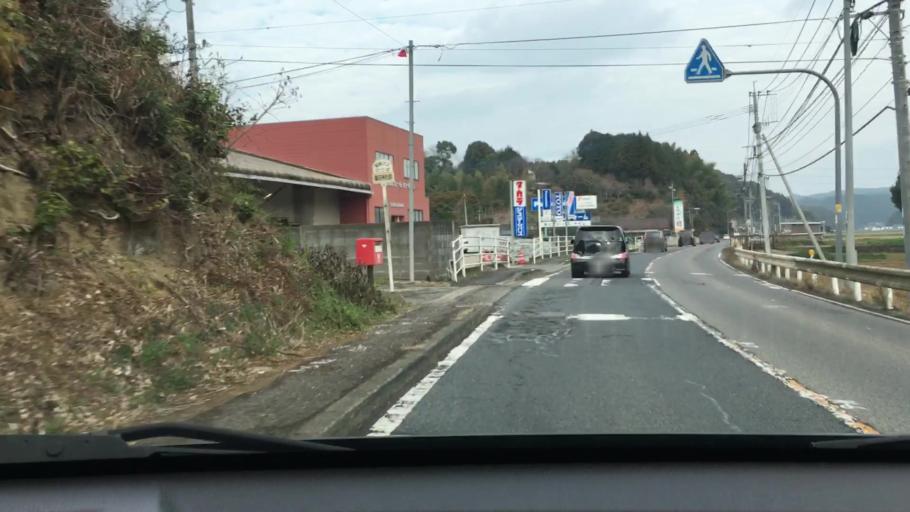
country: JP
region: Saga Prefecture
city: Imaricho-ko
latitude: 33.3003
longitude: 129.9183
